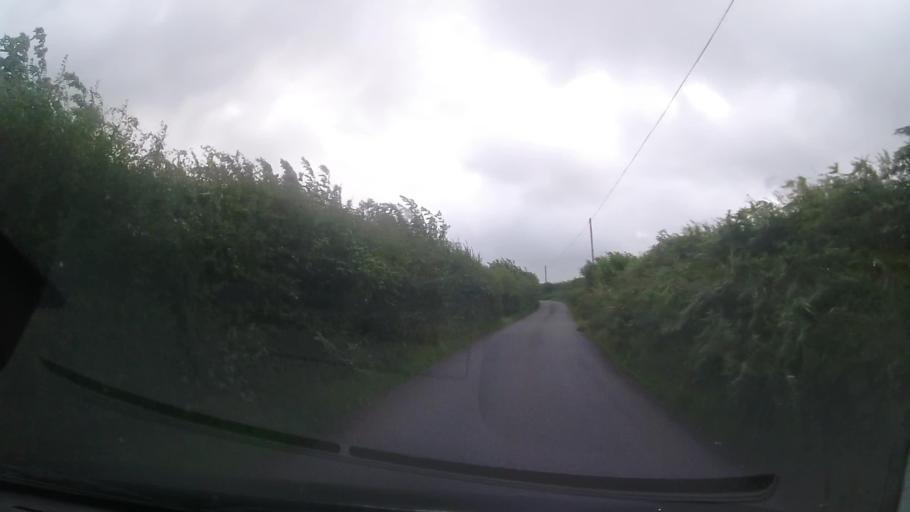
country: GB
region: Wales
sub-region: Sir Powys
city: Knighton
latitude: 52.3337
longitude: -3.0211
